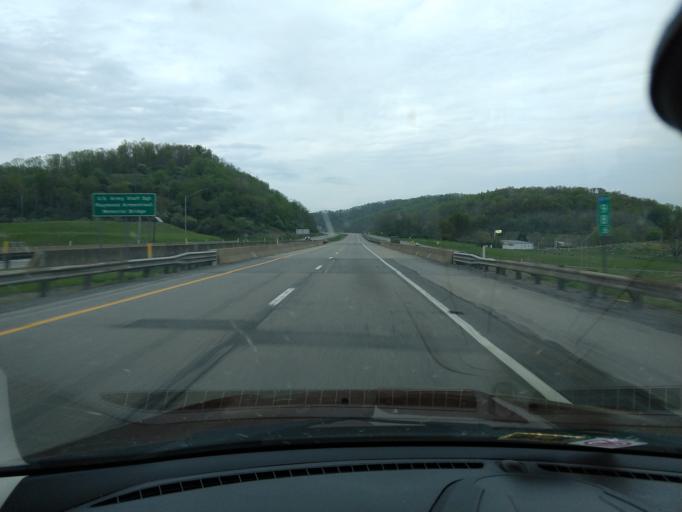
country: US
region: West Virginia
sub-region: Lewis County
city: Weston
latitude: 39.0211
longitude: -80.4278
